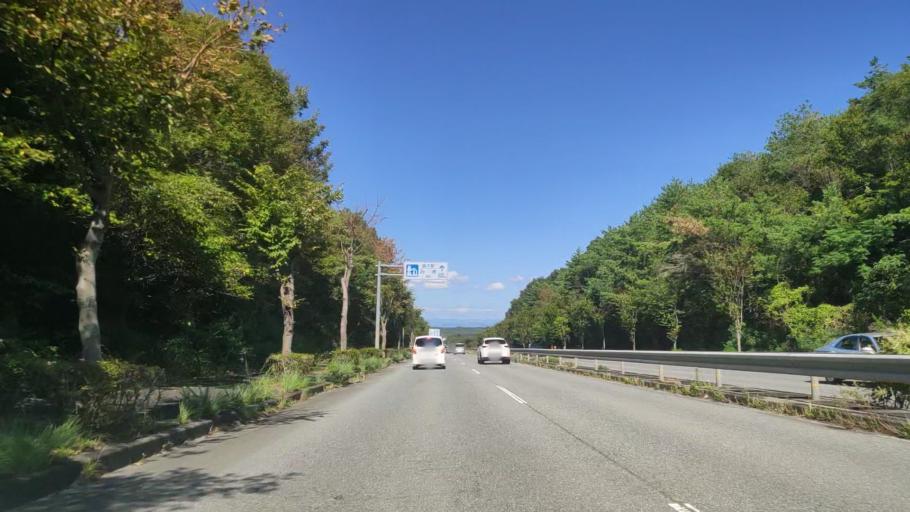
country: JP
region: Hyogo
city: Miki
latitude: 34.7832
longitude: 134.9796
